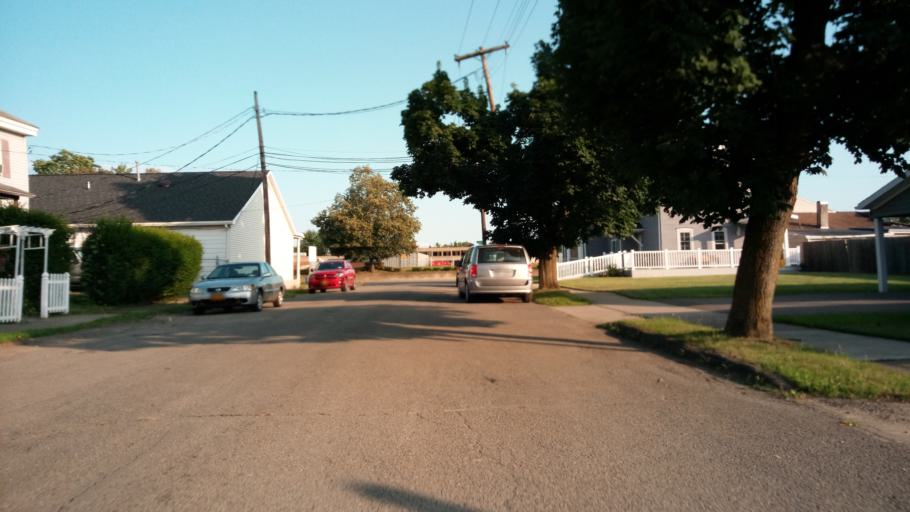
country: US
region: New York
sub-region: Chemung County
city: Elmira
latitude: 42.0943
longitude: -76.7956
